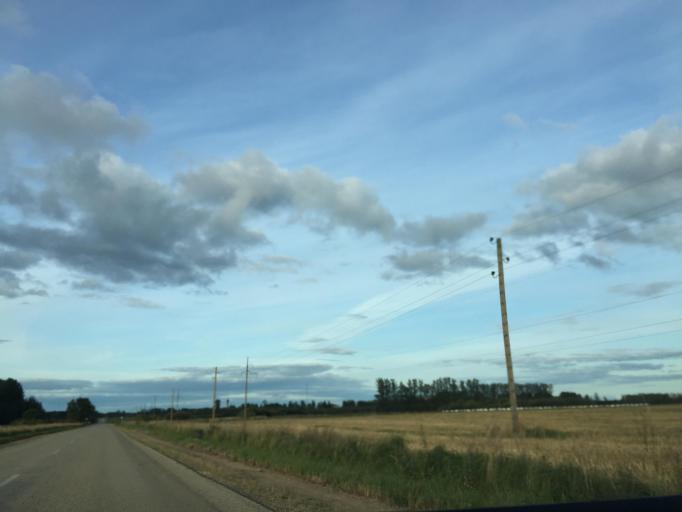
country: LV
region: Nereta
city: Nereta
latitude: 56.2691
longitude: 25.3722
